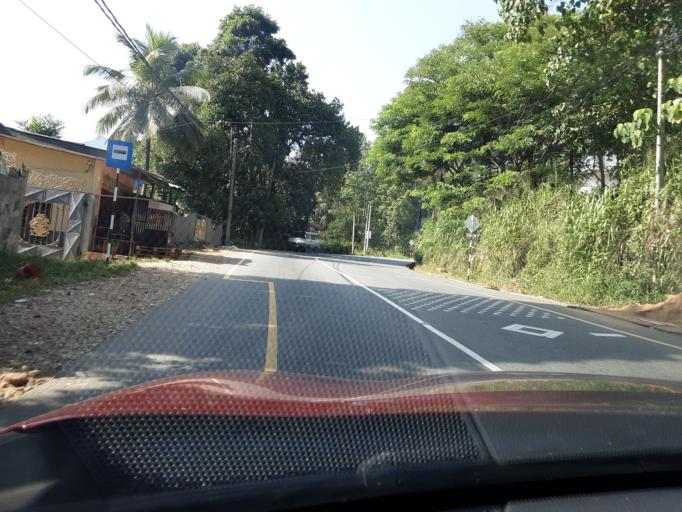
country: LK
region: Uva
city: Badulla
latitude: 6.9828
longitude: 81.0796
